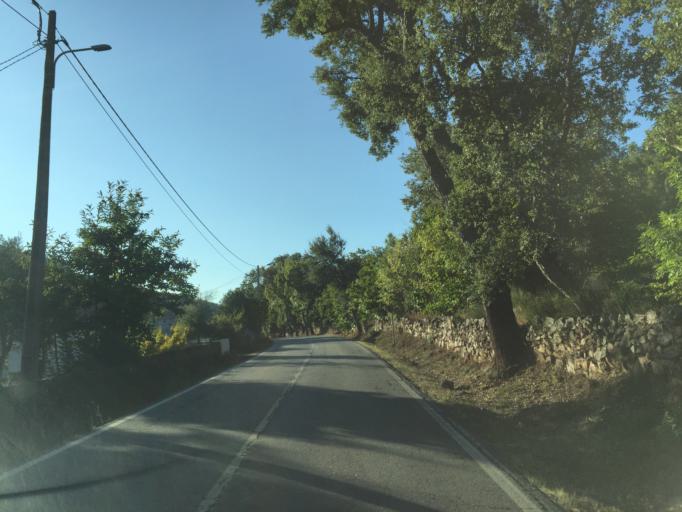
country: PT
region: Portalegre
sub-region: Marvao
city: Marvao
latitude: 39.3944
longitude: -7.4190
